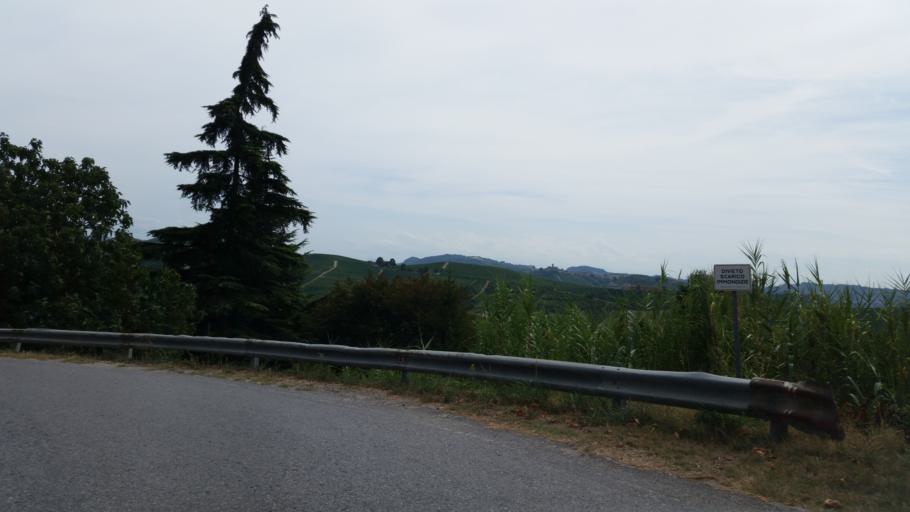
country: IT
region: Piedmont
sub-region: Provincia di Cuneo
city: Grinzane Cavour
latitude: 44.6535
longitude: 7.9922
